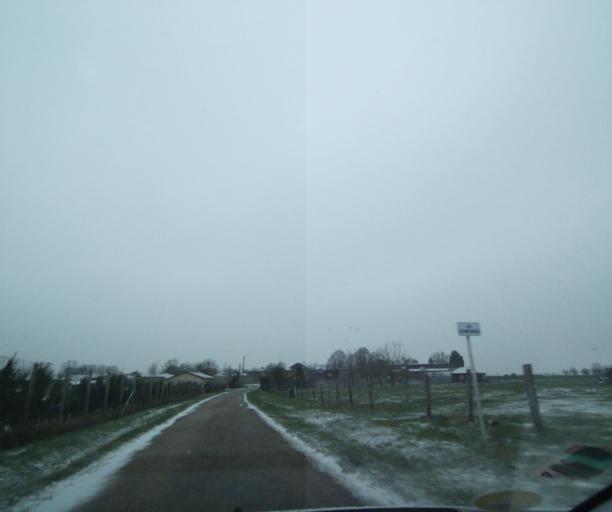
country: FR
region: Champagne-Ardenne
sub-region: Departement de la Haute-Marne
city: Wassy
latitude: 48.4689
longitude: 4.9964
